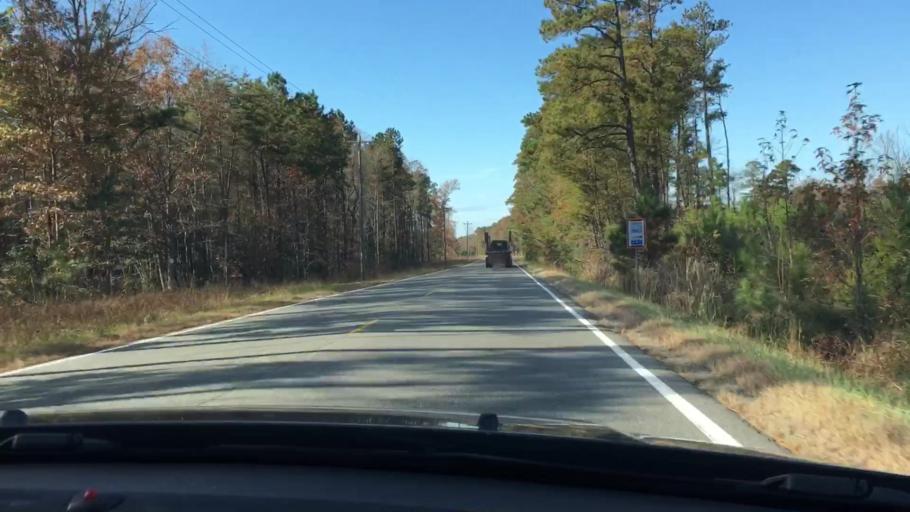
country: US
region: Virginia
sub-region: Hanover County
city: Hanover
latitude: 37.8198
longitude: -77.3210
